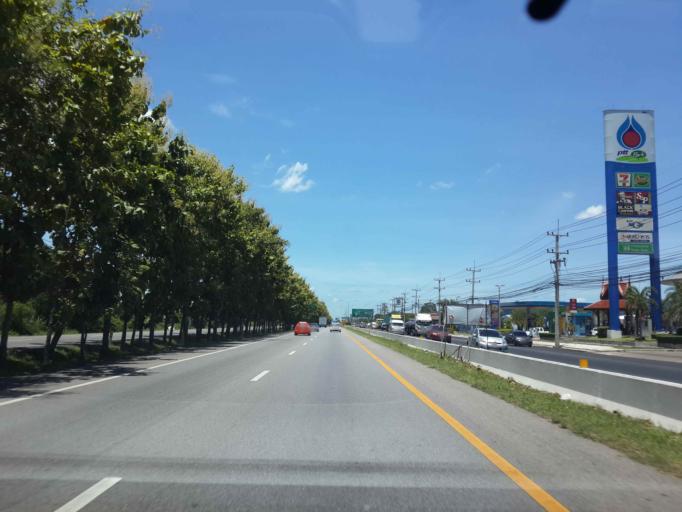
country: TH
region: Phetchaburi
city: Khao Yoi
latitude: 13.3040
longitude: 99.8246
